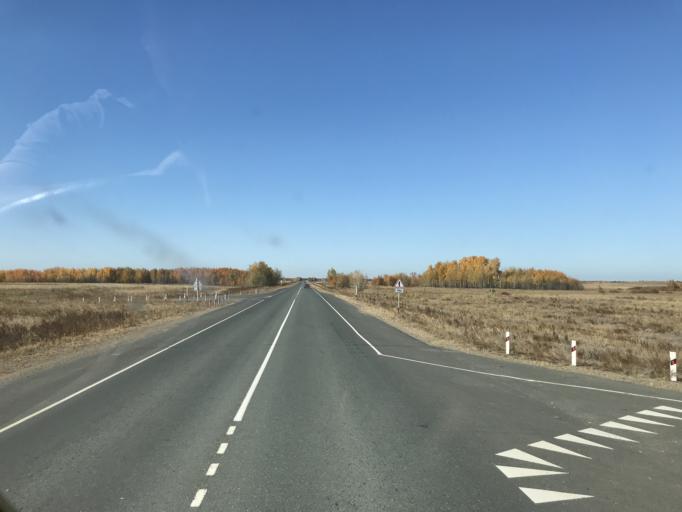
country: KZ
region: East Kazakhstan
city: Semey
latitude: 50.7072
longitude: 79.7334
